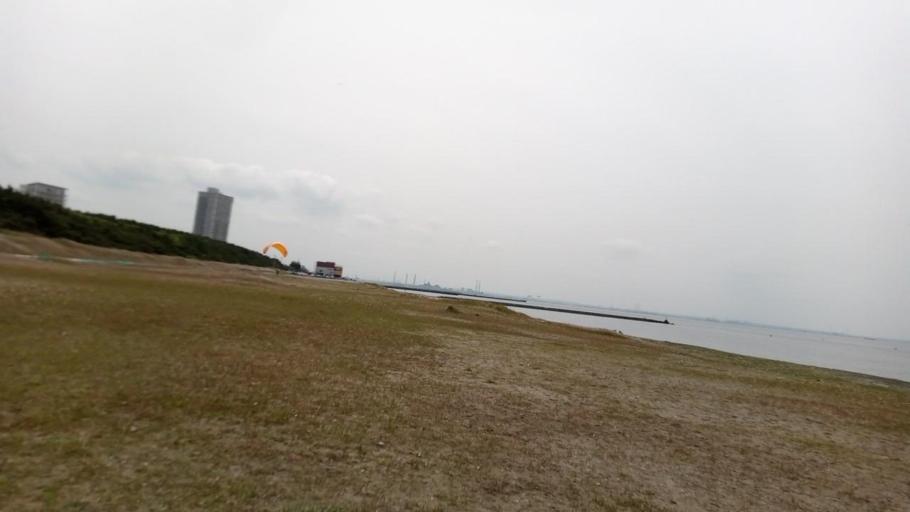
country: JP
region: Chiba
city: Funabashi
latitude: 35.6402
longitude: 140.0345
